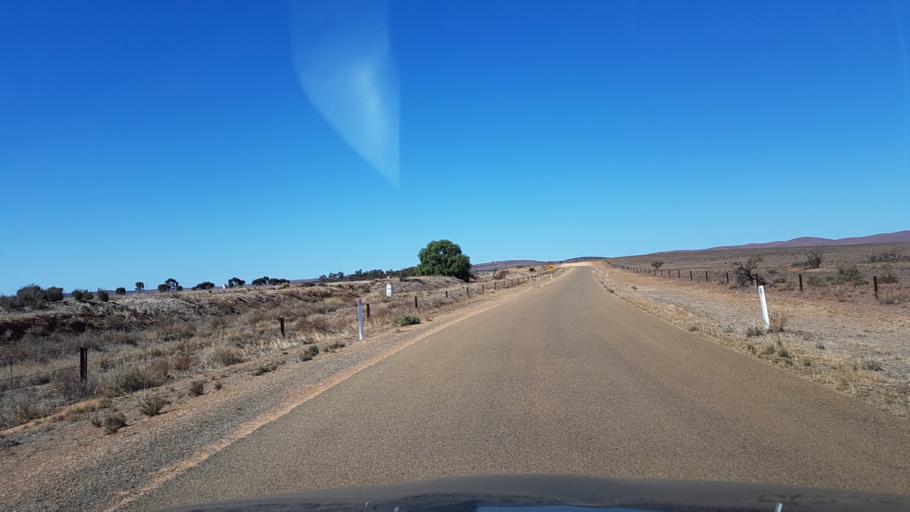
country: AU
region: South Australia
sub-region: Peterborough
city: Peterborough
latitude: -32.9728
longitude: 138.8547
